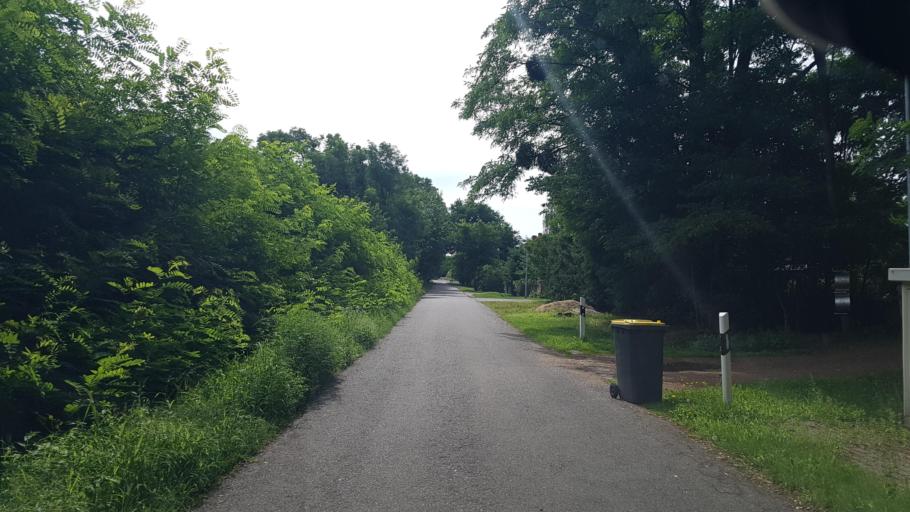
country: DE
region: Brandenburg
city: Drebkau
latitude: 51.6214
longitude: 14.2655
